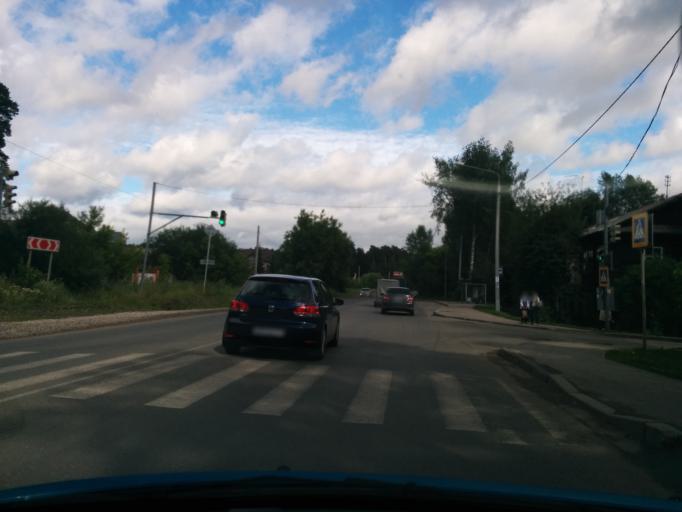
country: RU
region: Perm
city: Kondratovo
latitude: 58.0401
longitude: 56.1253
